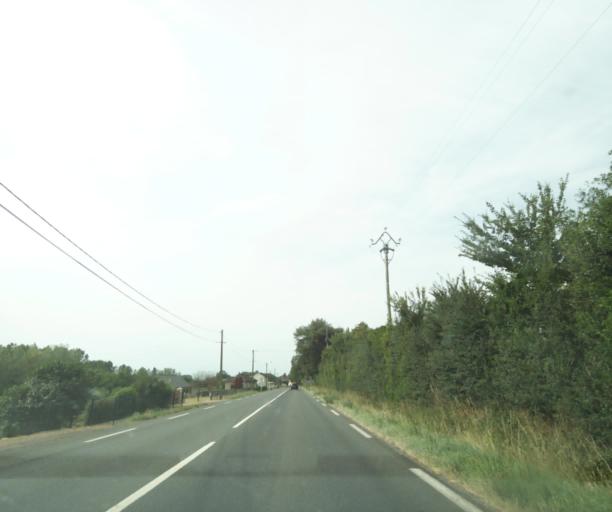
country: FR
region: Centre
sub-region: Departement d'Indre-et-Loire
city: Saint-Christophe-sur-le-Nais
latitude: 47.6606
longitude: 0.4769
